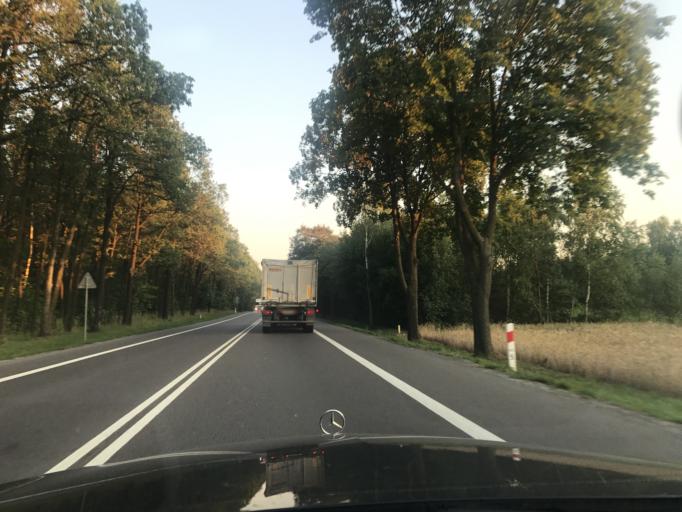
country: PL
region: Lublin Voivodeship
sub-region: Powiat lubelski
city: Niemce
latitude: 51.3971
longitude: 22.6368
